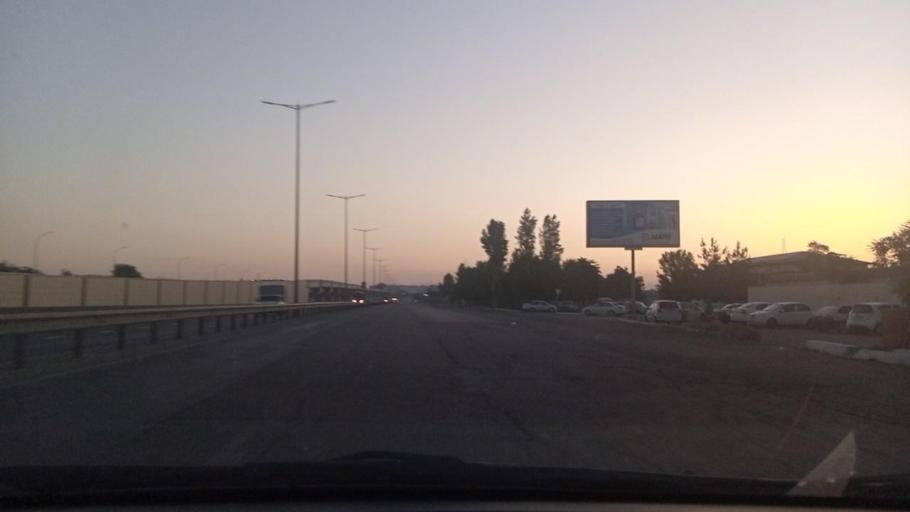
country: UZ
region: Toshkent Shahri
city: Bektemir
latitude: 41.2582
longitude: 69.3602
